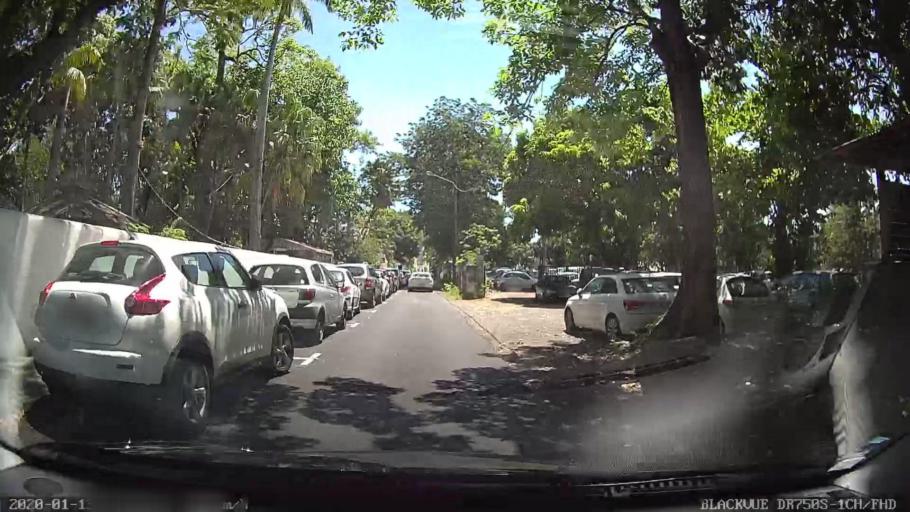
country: RE
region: Reunion
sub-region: Reunion
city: Saint-Denis
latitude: -20.8880
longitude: 55.4507
